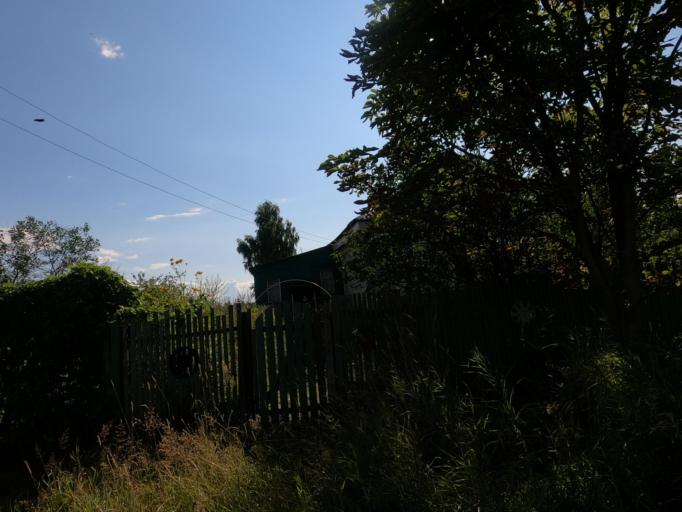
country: RU
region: Moskovskaya
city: Konobeyevo
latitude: 55.4117
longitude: 38.6962
